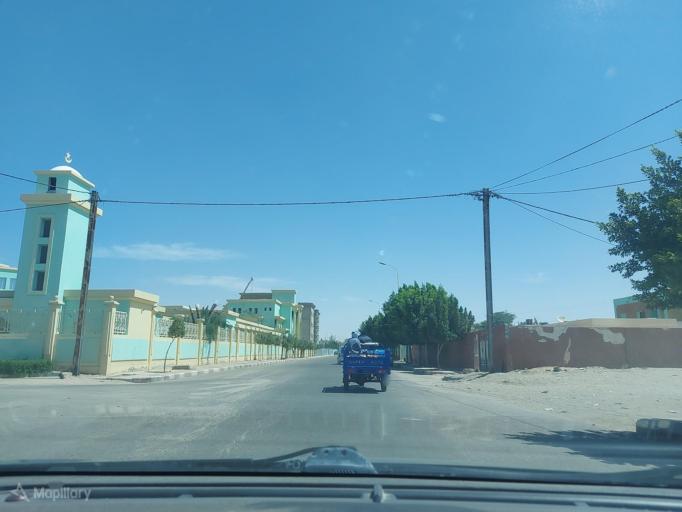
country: MR
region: Nouakchott
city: Nouakchott
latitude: 18.0844
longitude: -15.9721
